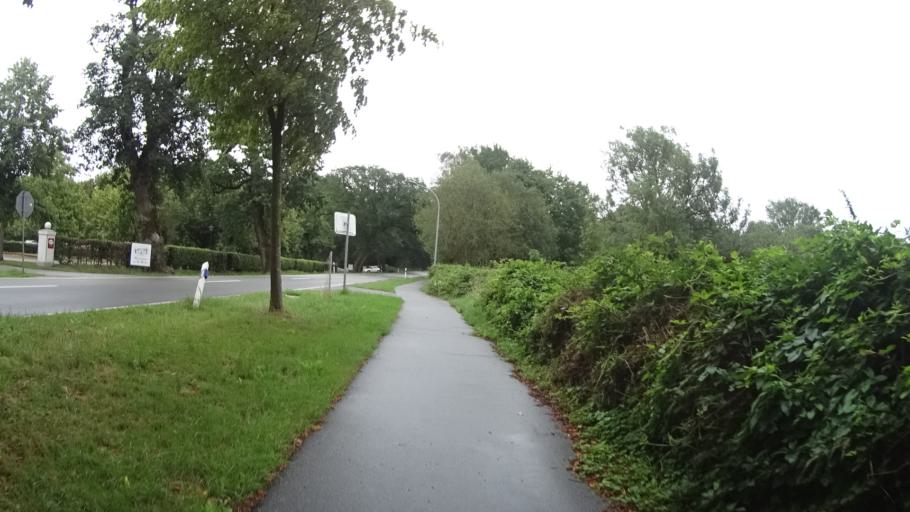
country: DE
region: Schleswig-Holstein
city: Alveslohe
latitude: 53.7846
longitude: 9.9453
